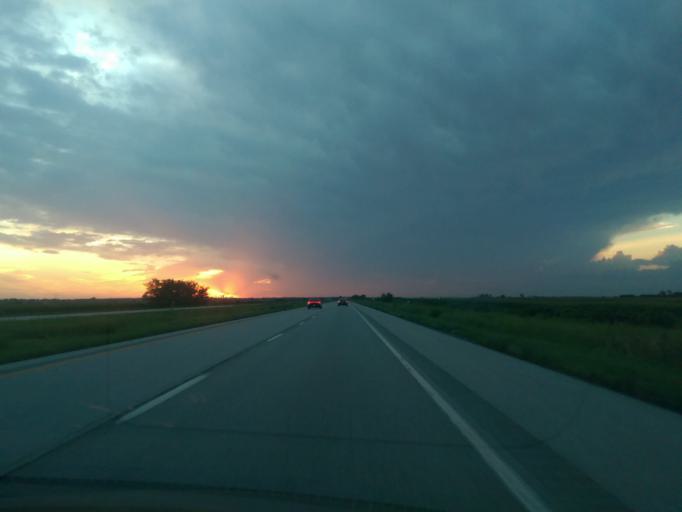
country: US
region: Iowa
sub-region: Fremont County
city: Hamburg
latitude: 40.6315
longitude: -95.7201
